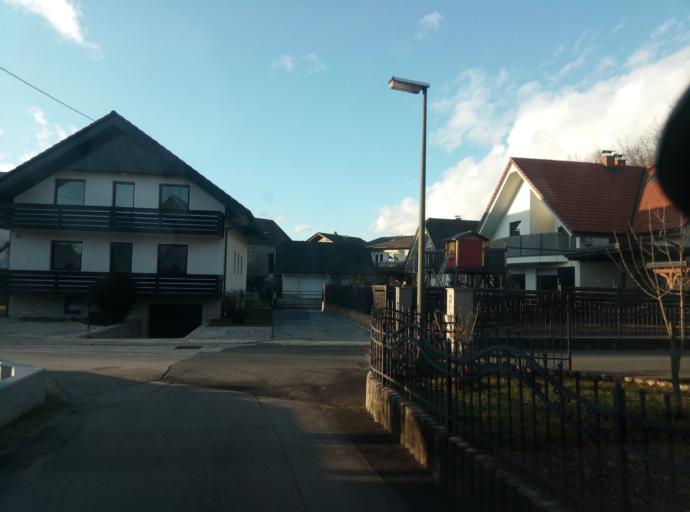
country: SI
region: Sencur
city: Hrastje
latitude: 46.2241
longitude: 14.3799
